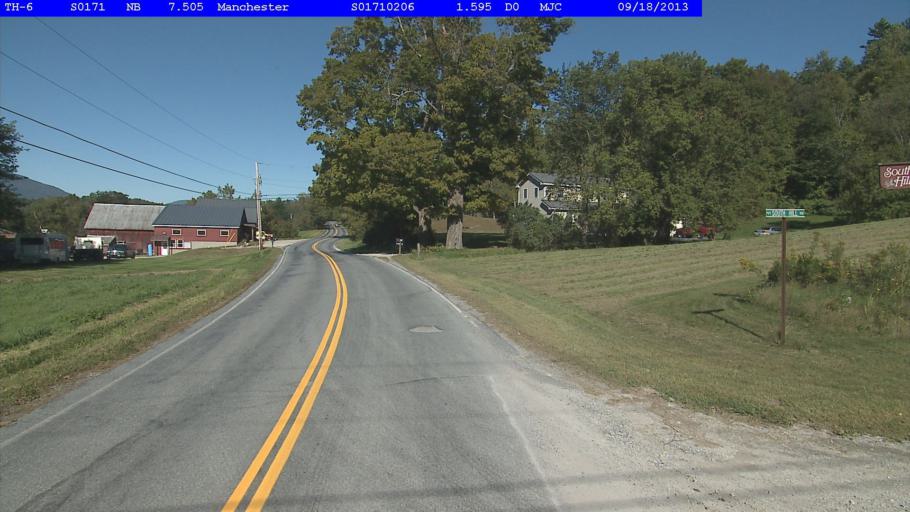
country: US
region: Vermont
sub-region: Bennington County
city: Manchester Center
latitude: 43.1325
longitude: -73.0708
